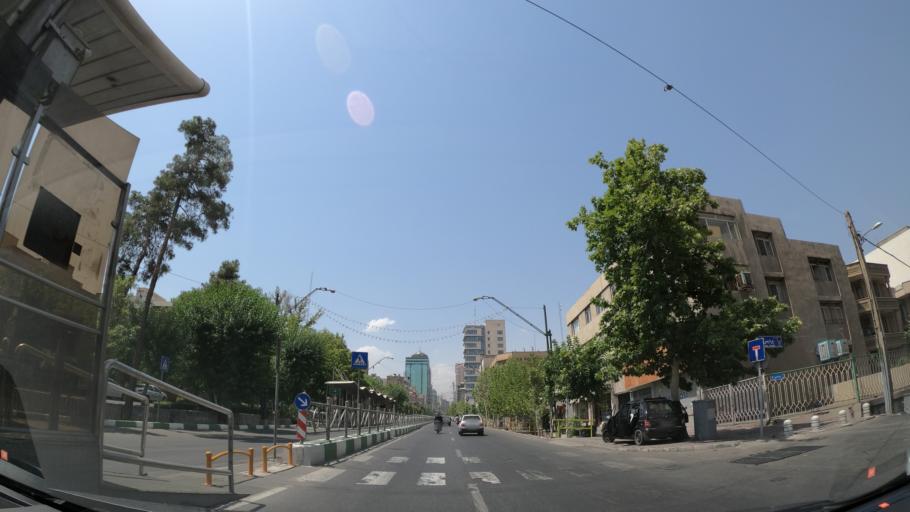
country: IR
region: Tehran
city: Tehran
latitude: 35.7283
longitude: 51.4131
